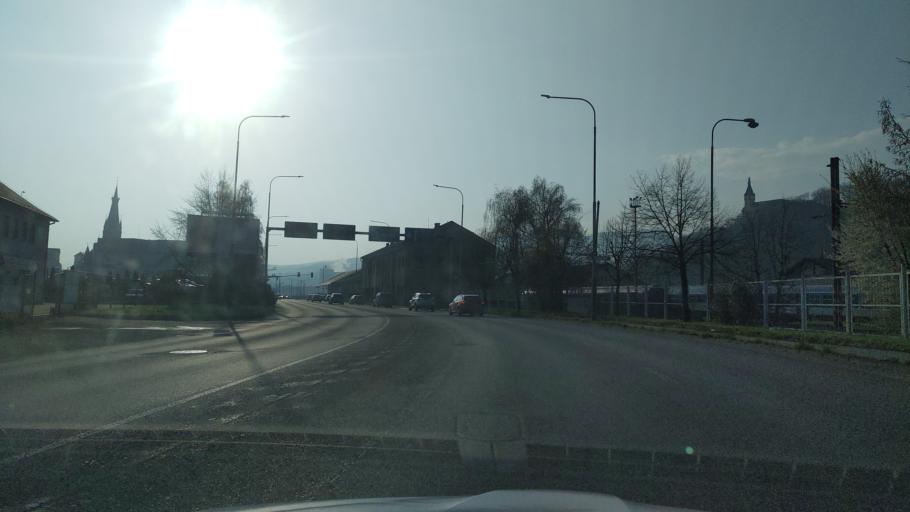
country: CZ
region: Ustecky
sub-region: Okres Usti nad Labem
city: Usti nad Labem
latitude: 50.6587
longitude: 14.0338
